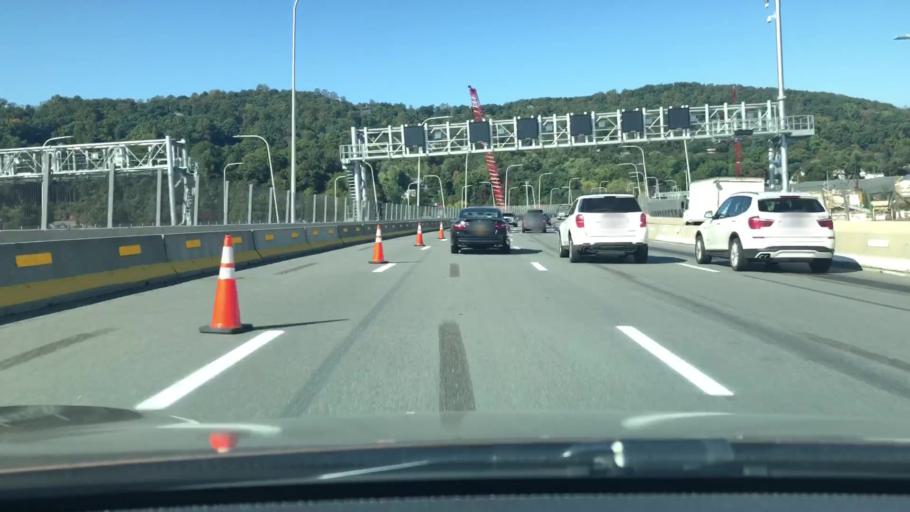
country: US
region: New York
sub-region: Rockland County
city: South Nyack
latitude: 41.0717
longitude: -73.9146
